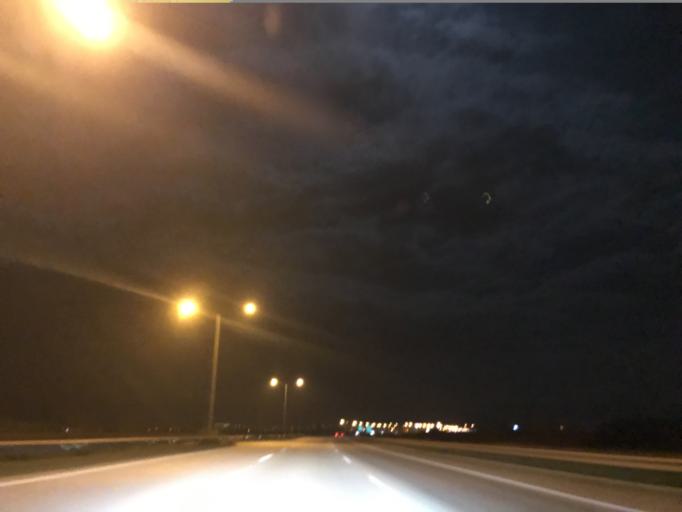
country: TR
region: Hatay
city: Mahmutlar
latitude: 36.9576
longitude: 36.1471
